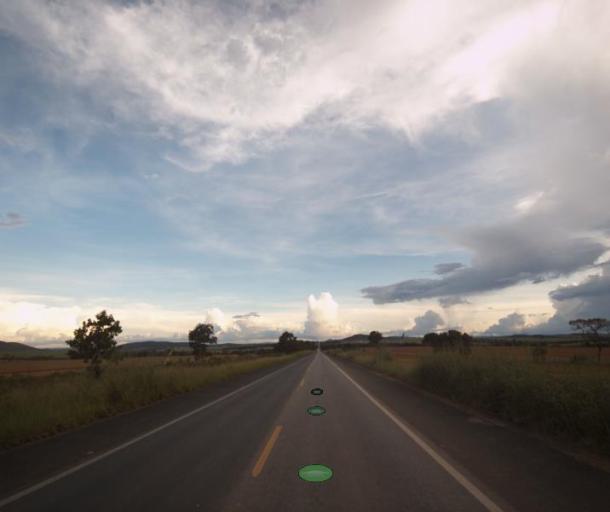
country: BR
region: Goias
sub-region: Uruacu
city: Uruacu
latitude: -14.1744
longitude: -49.1251
